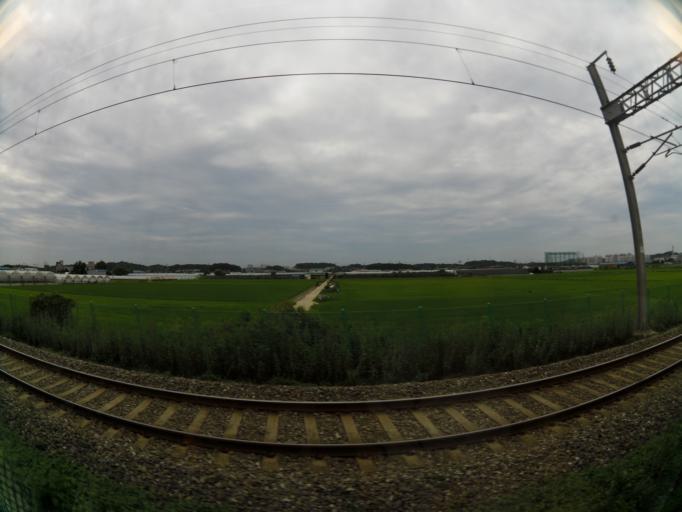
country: KR
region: Gyeonggi-do
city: Osan
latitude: 37.1254
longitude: 127.0641
